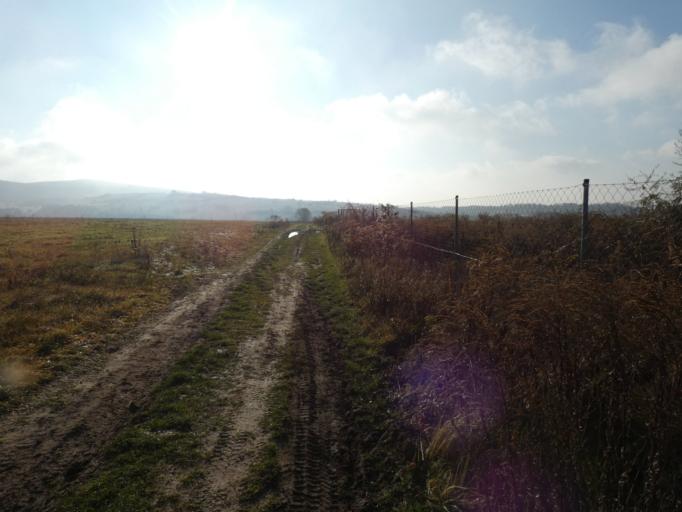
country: HU
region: Pest
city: Paty
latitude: 47.5062
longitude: 18.8337
